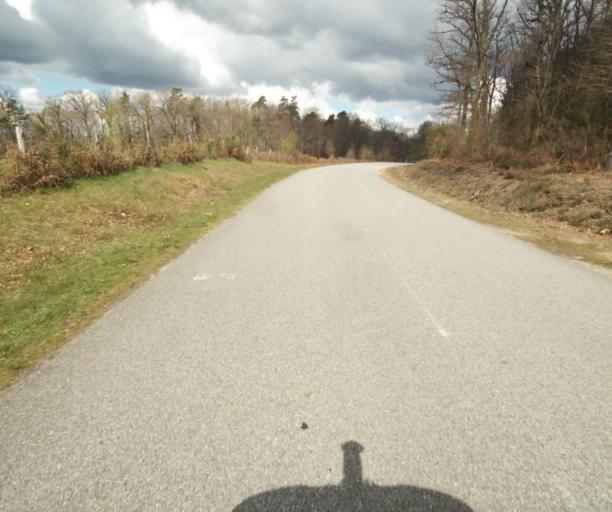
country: FR
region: Limousin
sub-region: Departement de la Correze
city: Correze
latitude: 45.2975
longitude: 1.8932
